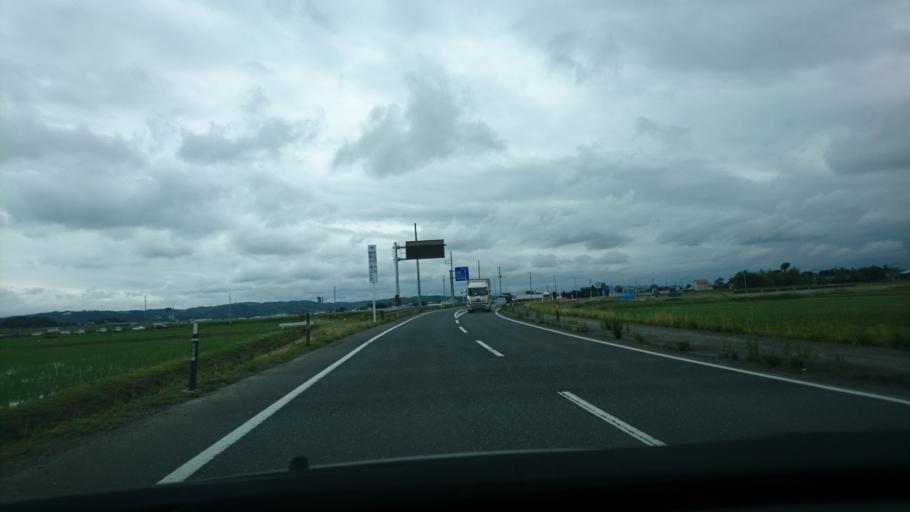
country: JP
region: Miyagi
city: Wakuya
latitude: 38.6795
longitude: 141.2611
